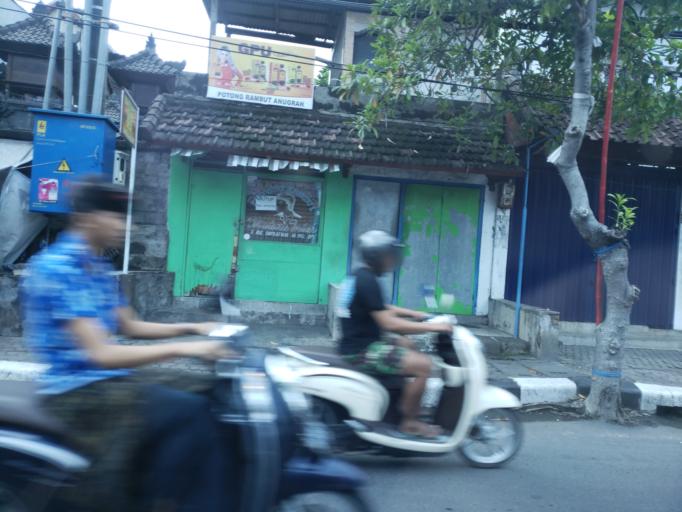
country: ID
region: Bali
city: Dajan Tangluk
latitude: -8.6483
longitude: 115.2382
